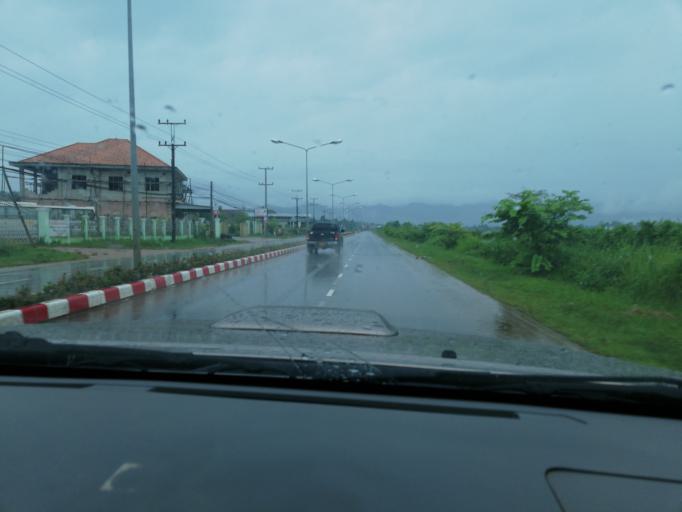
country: LA
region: Loungnamtha
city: Louang Namtha
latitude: 20.9604
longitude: 101.4039
